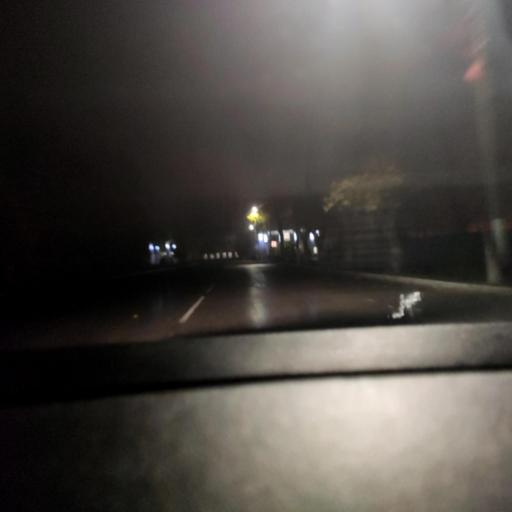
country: RU
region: Voronezj
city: Semiluki
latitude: 51.6865
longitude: 39.0378
